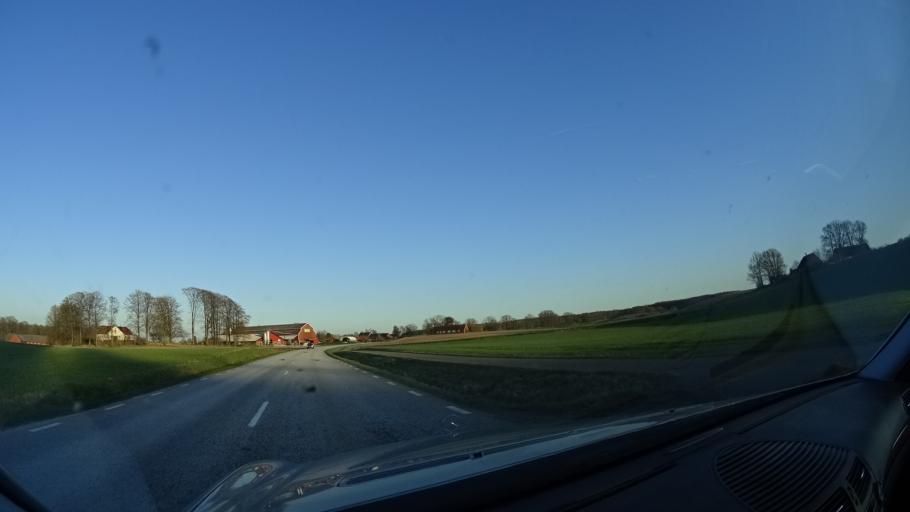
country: SE
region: Skane
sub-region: Eslovs Kommun
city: Stehag
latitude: 55.9509
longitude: 13.3485
